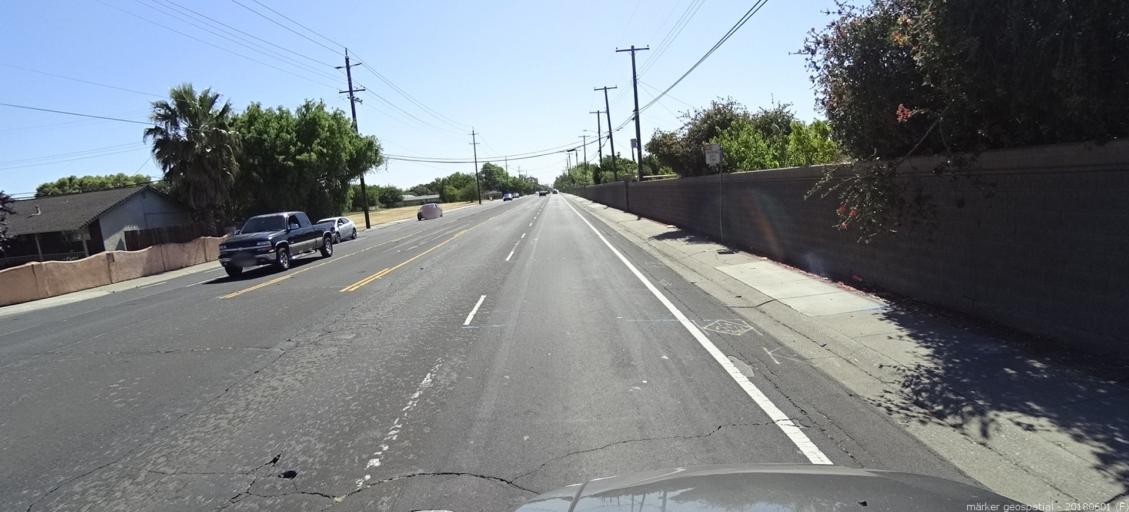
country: US
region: California
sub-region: Sacramento County
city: Parkway
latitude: 38.4813
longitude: -121.4990
